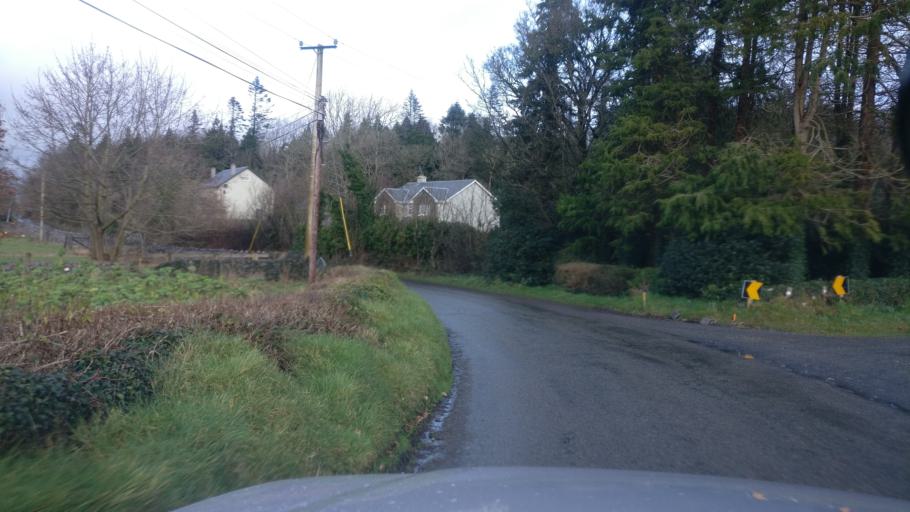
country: IE
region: Connaught
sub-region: County Galway
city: Athenry
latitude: 53.2503
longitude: -8.7190
